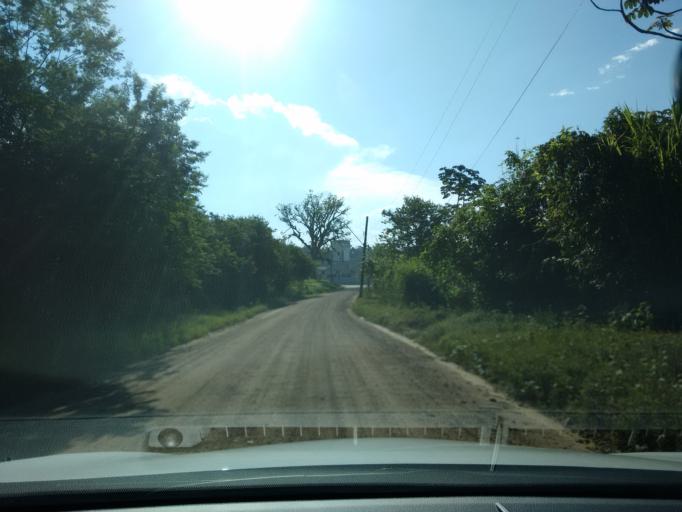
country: BR
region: Santa Catarina
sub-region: Blumenau
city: Blumenau
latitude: -26.8993
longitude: -49.0741
